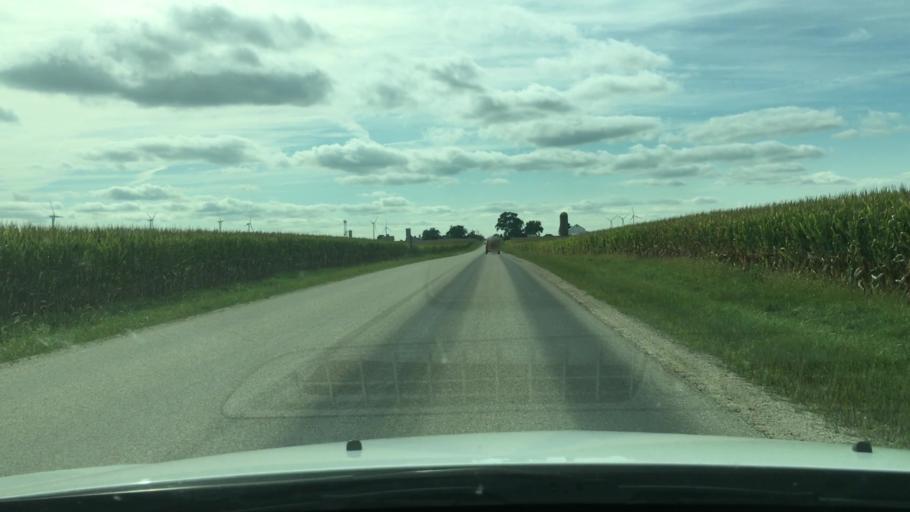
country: US
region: Illinois
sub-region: DeKalb County
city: Malta
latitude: 41.8492
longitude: -88.8883
